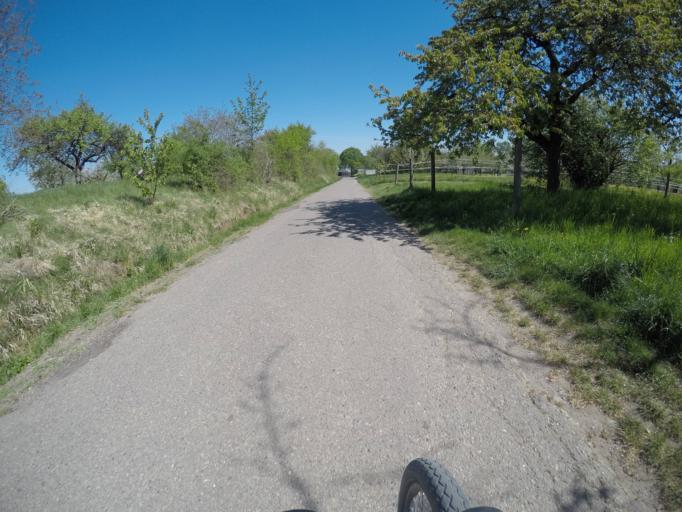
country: DE
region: Baden-Wuerttemberg
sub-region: Regierungsbezirk Stuttgart
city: Waiblingen
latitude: 48.8004
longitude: 9.3140
